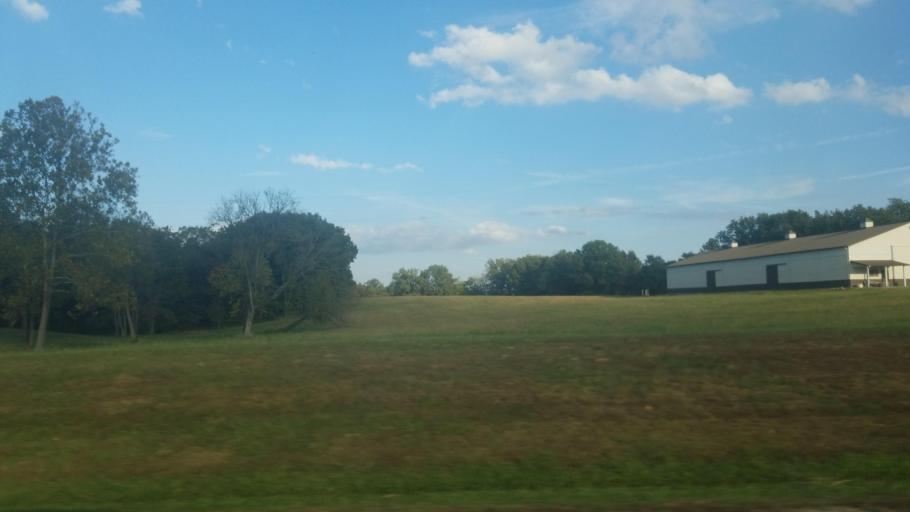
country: US
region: Illinois
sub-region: Saline County
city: Harrisburg
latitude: 37.8111
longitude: -88.6146
